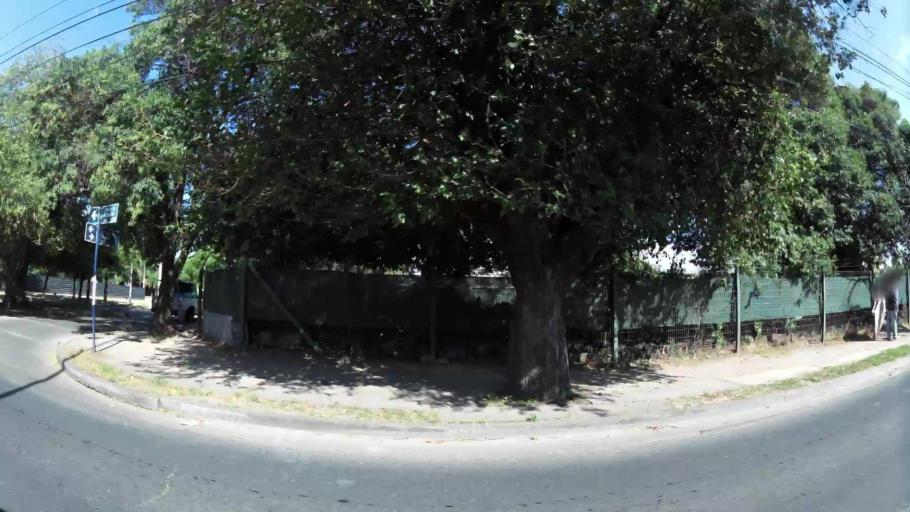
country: AR
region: Cordoba
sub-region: Departamento de Capital
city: Cordoba
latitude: -31.4615
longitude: -64.1868
